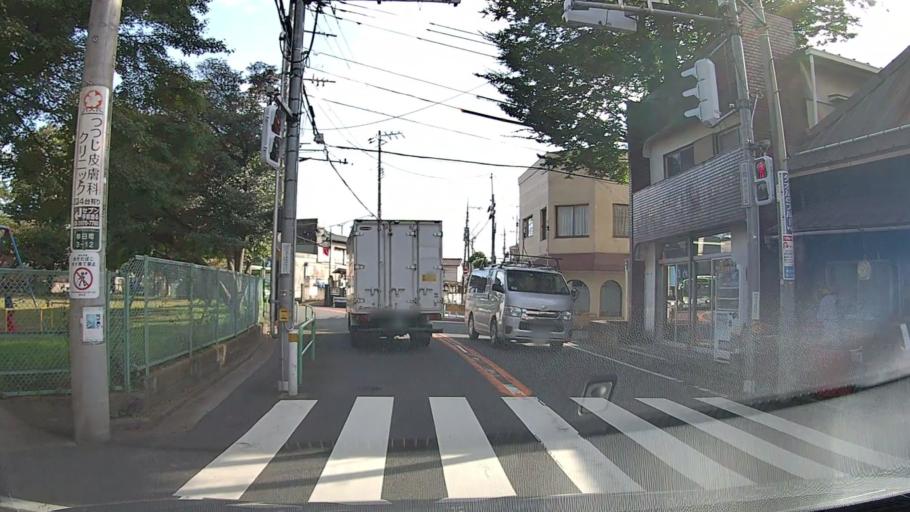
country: JP
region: Saitama
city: Wako
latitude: 35.7497
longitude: 139.6402
